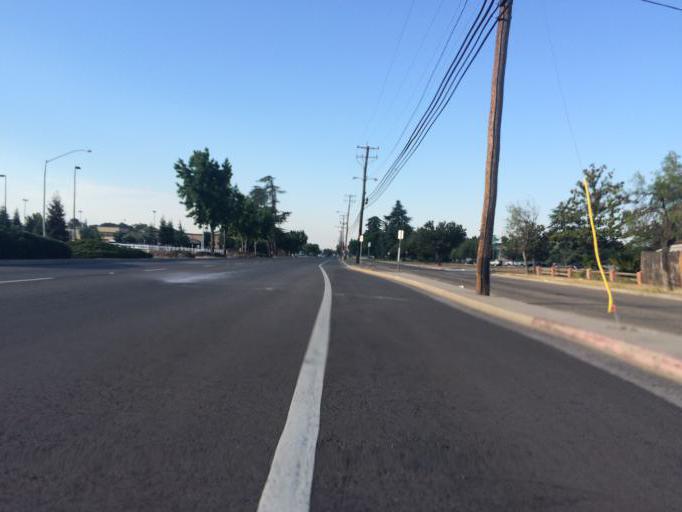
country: US
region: California
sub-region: Fresno County
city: Fresno
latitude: 36.7922
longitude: -119.7544
